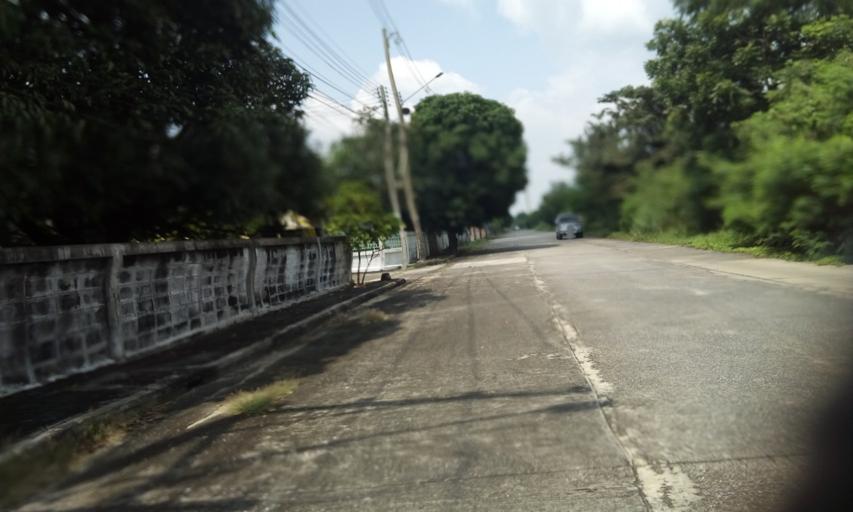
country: TH
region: Pathum Thani
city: Ban Rangsit
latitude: 14.0481
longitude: 100.8312
